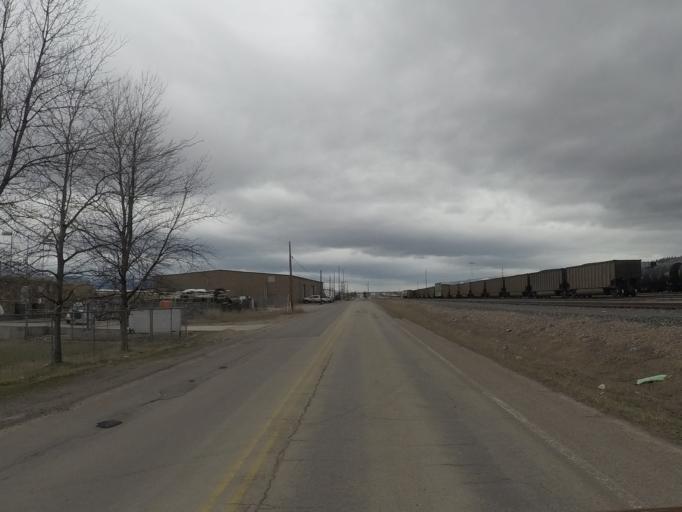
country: US
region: Montana
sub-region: Missoula County
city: Missoula
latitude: 46.8907
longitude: -114.0230
